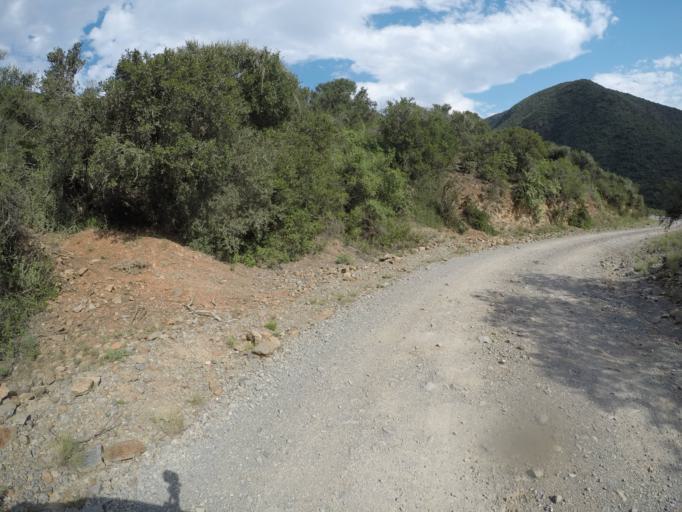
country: ZA
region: Eastern Cape
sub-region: Cacadu District Municipality
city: Kareedouw
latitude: -33.6482
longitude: 24.3384
